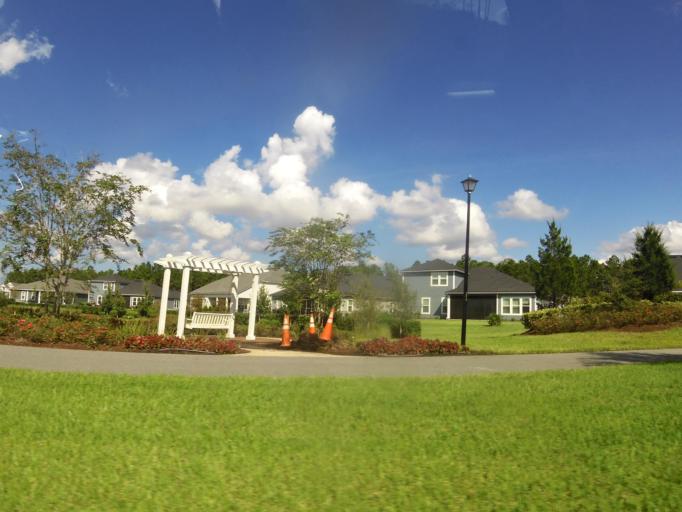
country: US
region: Florida
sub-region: Saint Johns County
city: Palm Valley
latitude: 30.0826
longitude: -81.4711
